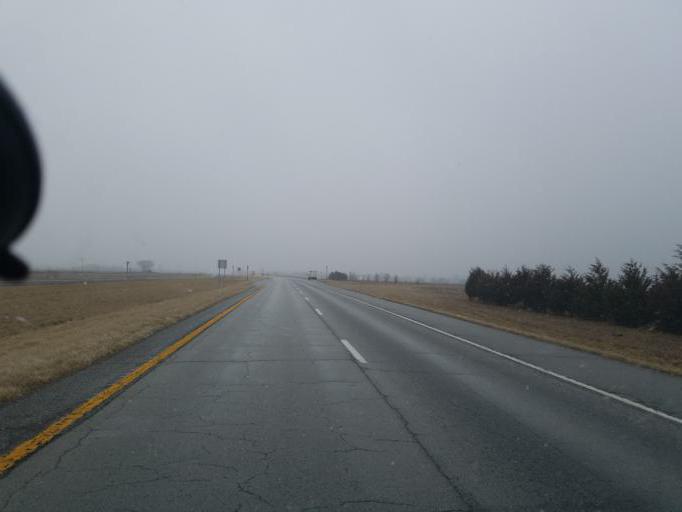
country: US
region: Missouri
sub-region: Macon County
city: La Plata
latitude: 39.9417
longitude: -92.4772
